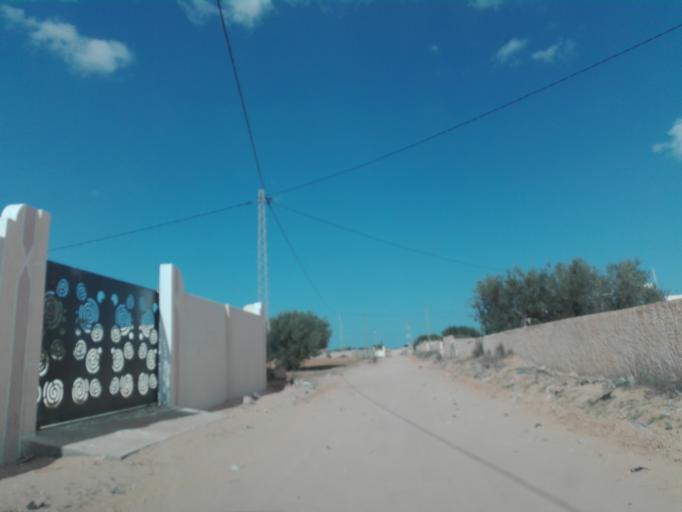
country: TN
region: Madanin
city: Bin Qirdan
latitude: 33.1617
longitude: 11.1953
